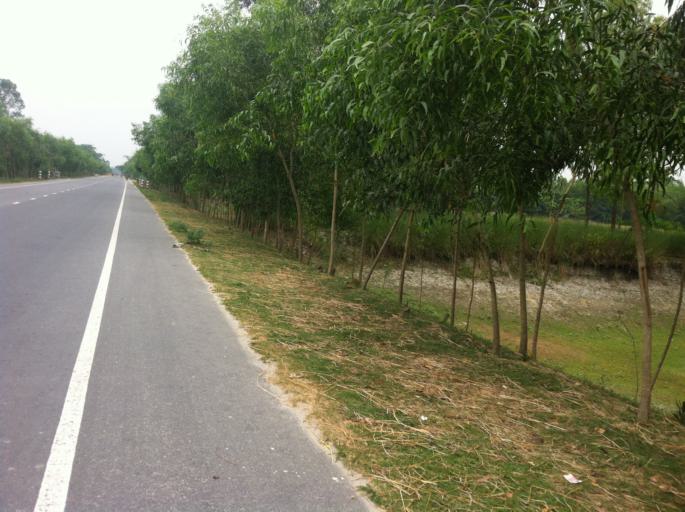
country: BD
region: Rangpur Division
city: Rangpur
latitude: 25.5775
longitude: 89.2649
